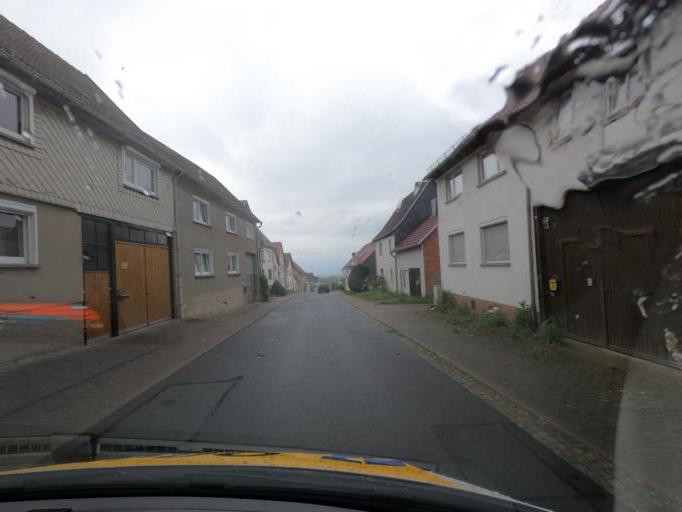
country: DE
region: Thuringia
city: Kleinbartloff
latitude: 51.3092
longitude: 10.4110
